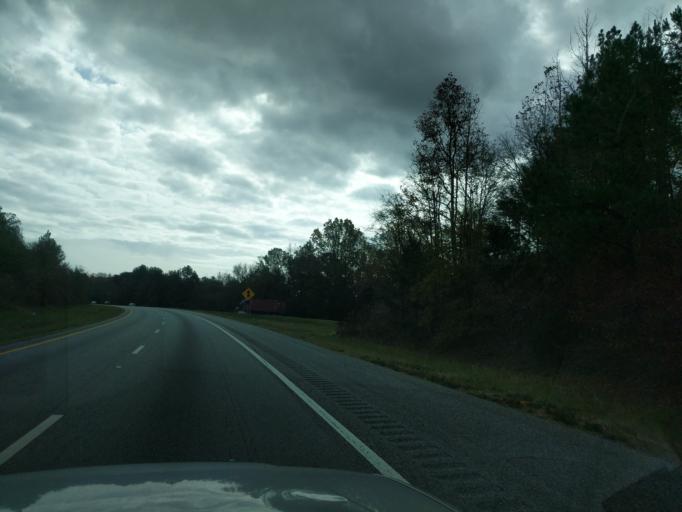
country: US
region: South Carolina
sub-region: Laurens County
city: Clinton
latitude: 34.5136
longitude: -81.8705
